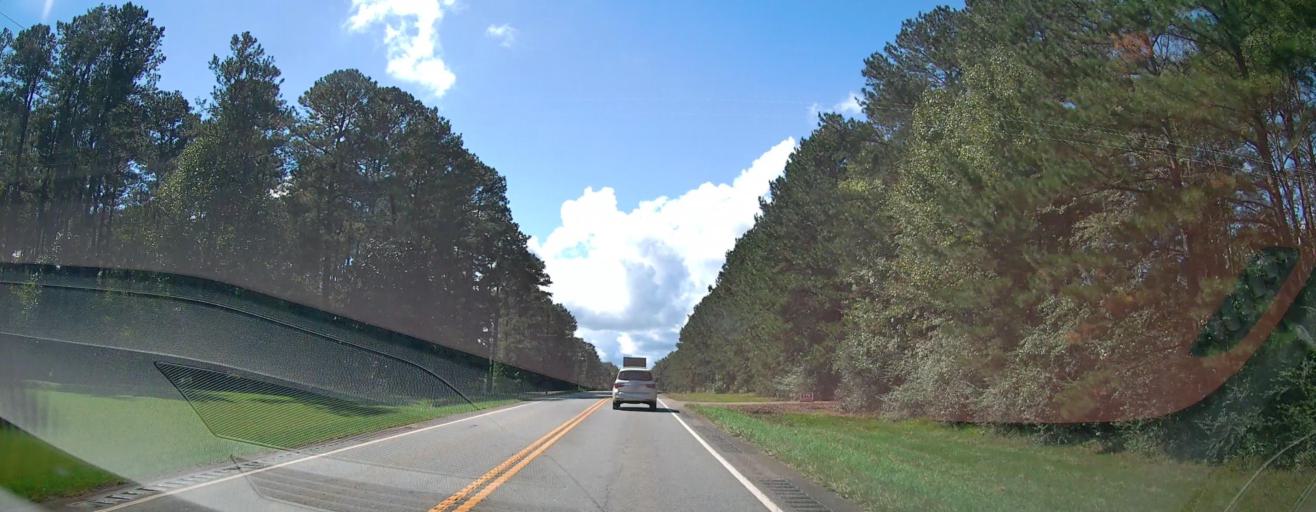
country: US
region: Georgia
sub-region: Jones County
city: Gray
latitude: 33.0384
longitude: -83.4064
